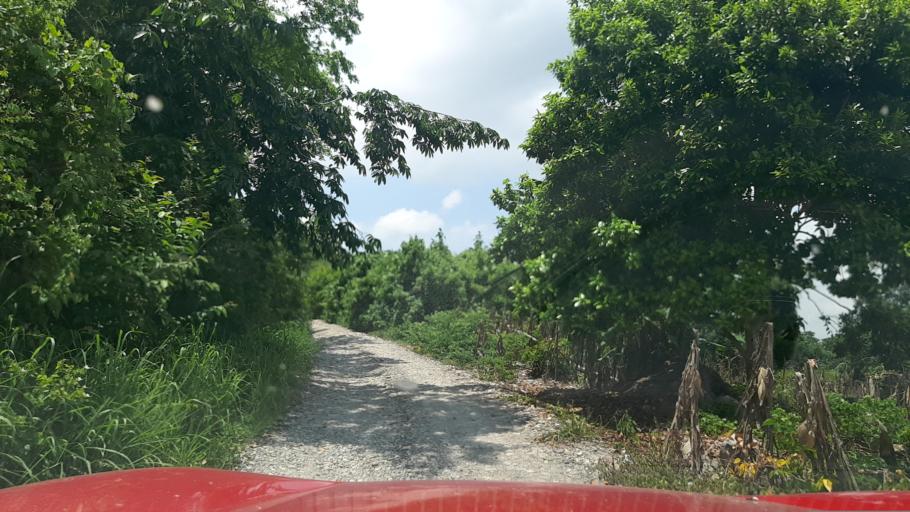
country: MX
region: Veracruz
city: Papantla de Olarte
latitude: 20.4240
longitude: -97.2674
